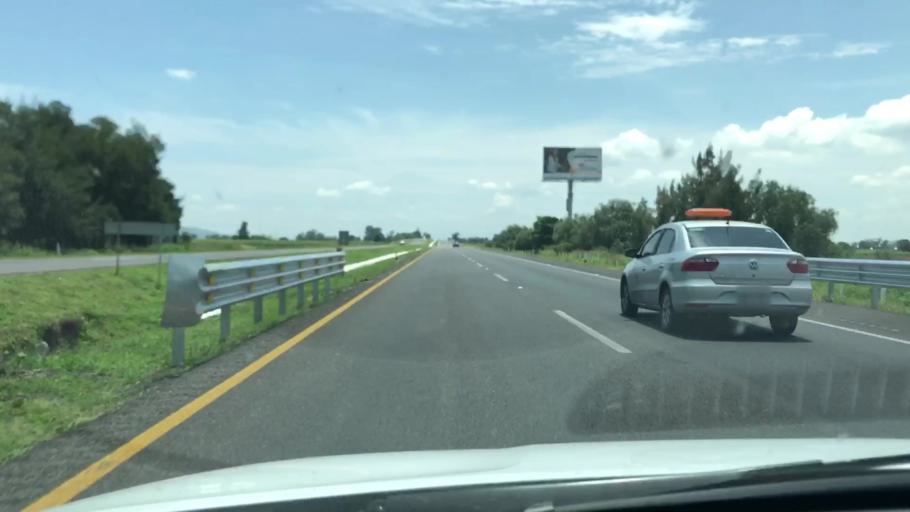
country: MX
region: Guanajuato
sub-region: Irapuato
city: Cuarta Brigada
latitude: 20.6487
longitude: -101.2798
